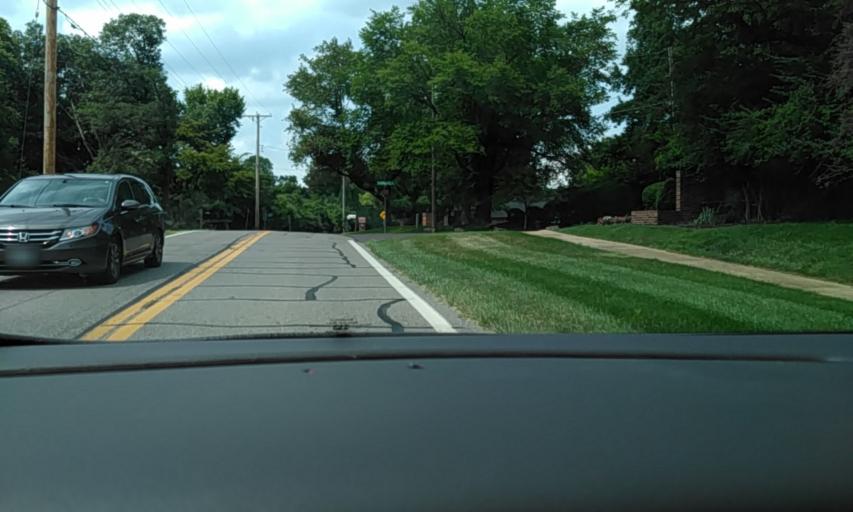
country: US
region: Missouri
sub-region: Saint Louis County
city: Town and Country
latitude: 38.6040
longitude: -90.4834
